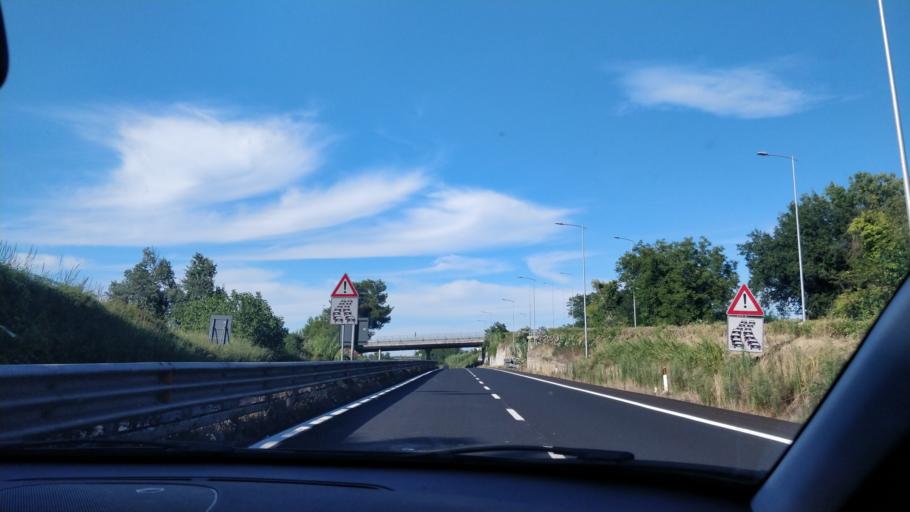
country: IT
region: Abruzzo
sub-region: Provincia di Chieti
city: Chieti
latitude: 42.3945
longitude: 14.1595
